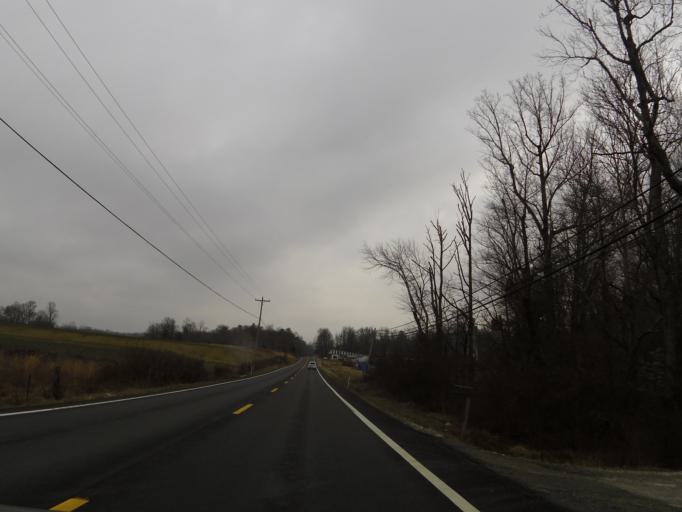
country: US
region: Tennessee
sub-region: Morgan County
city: Wartburg
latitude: 36.0945
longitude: -84.5762
